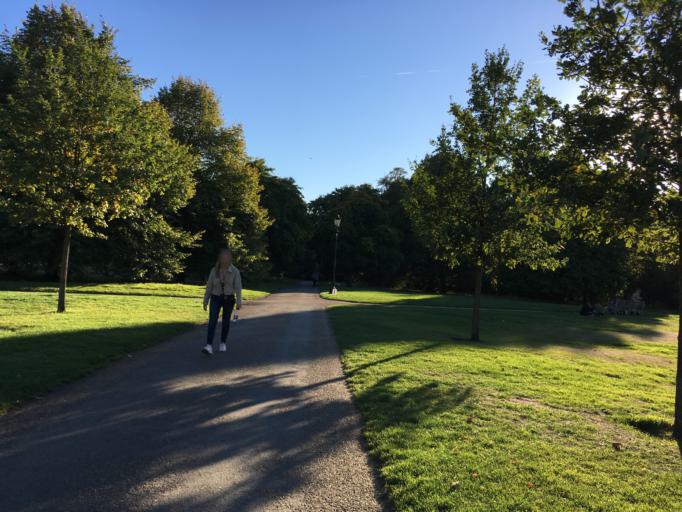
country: GB
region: England
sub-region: Greater London
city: Bayswater
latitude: 51.5098
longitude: -0.1634
